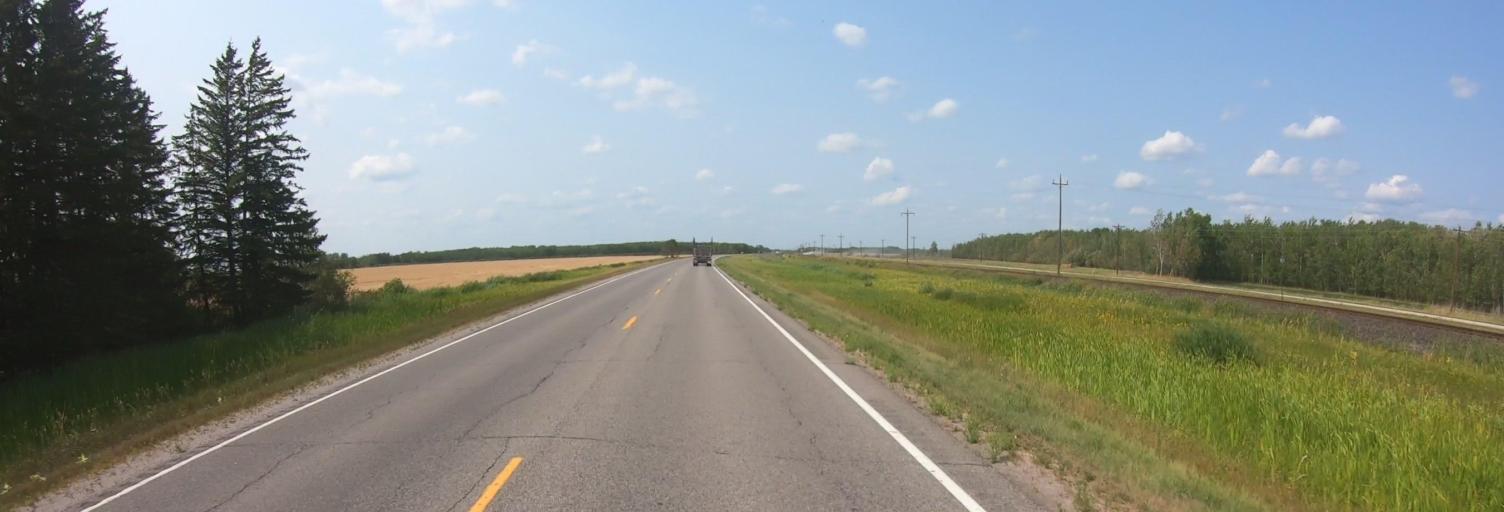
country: US
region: Minnesota
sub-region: Roseau County
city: Warroad
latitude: 48.8749
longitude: -95.2750
